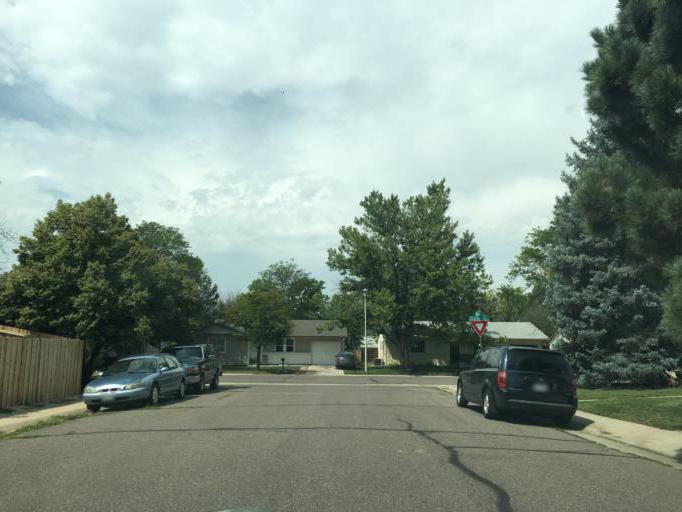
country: US
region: Colorado
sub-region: Adams County
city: Aurora
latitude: 39.7354
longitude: -104.7927
